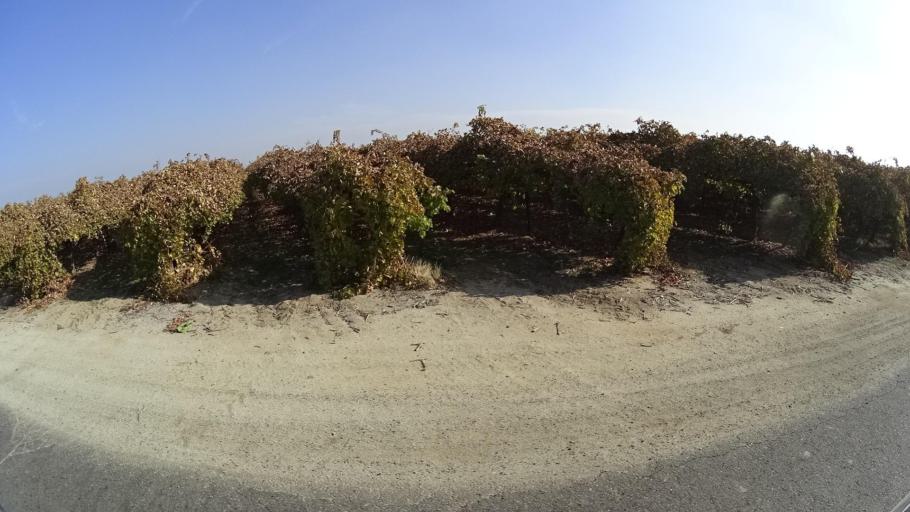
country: US
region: California
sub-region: Kern County
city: McFarland
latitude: 35.6859
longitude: -119.1794
